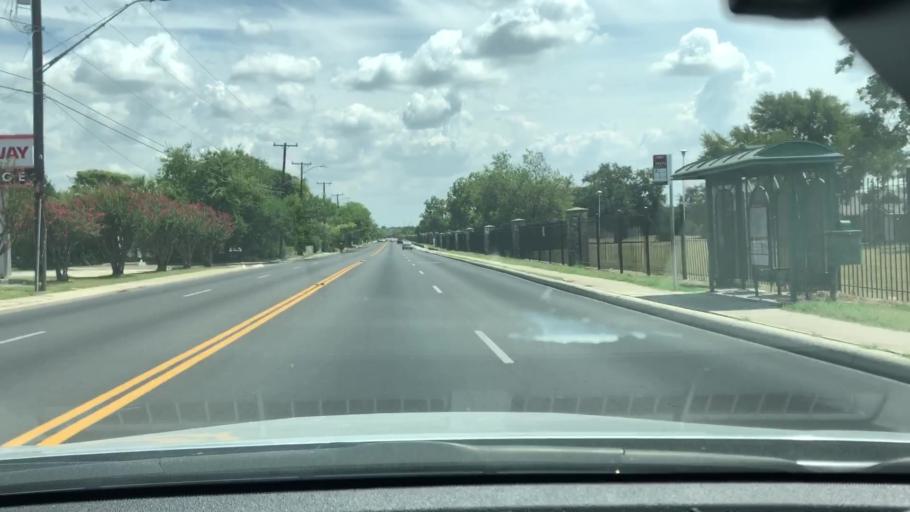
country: US
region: Texas
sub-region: Bexar County
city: Terrell Hills
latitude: 29.4848
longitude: -98.4274
